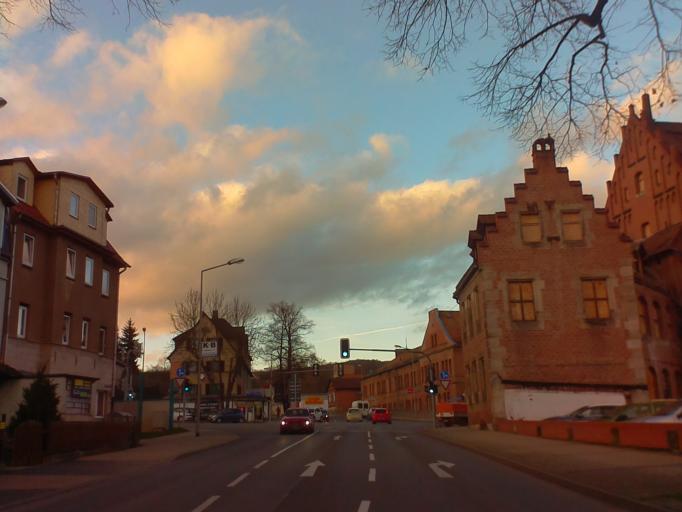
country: DE
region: Thuringia
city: Rudolstadt
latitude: 50.7124
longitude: 11.3191
